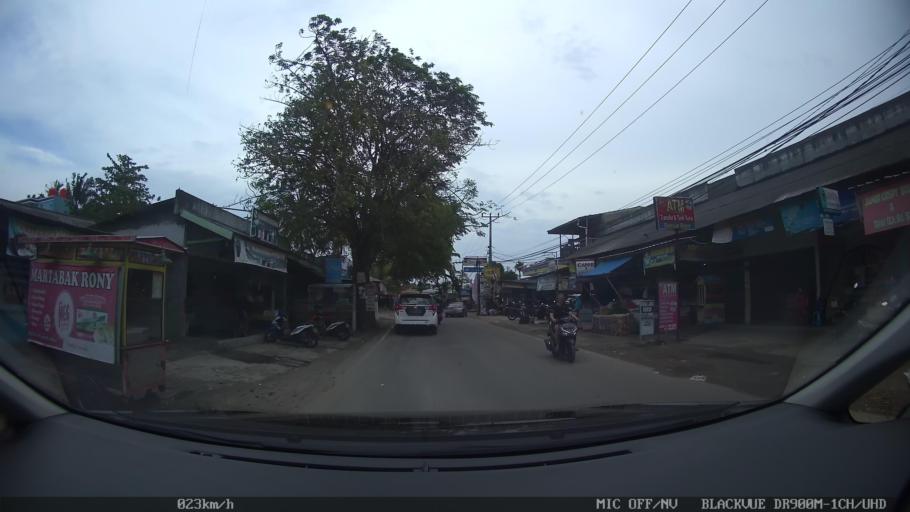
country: ID
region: Lampung
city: Kedaton
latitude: -5.3735
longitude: 105.2217
